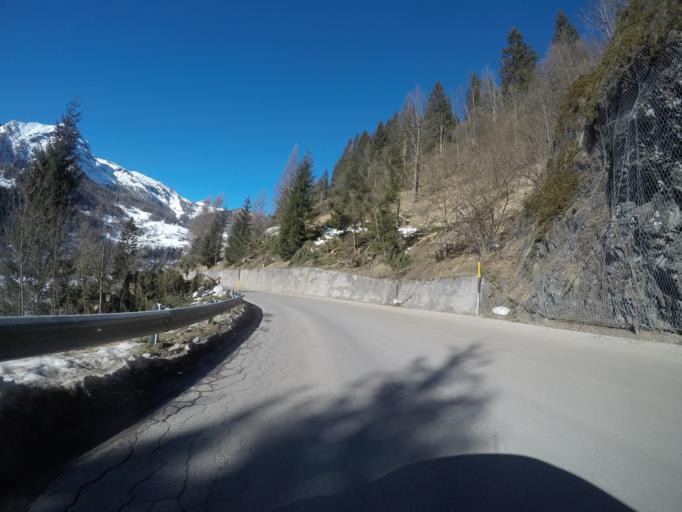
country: IT
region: Veneto
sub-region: Provincia di Belluno
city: Colle Santa Lucia
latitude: 46.4542
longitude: 11.9935
